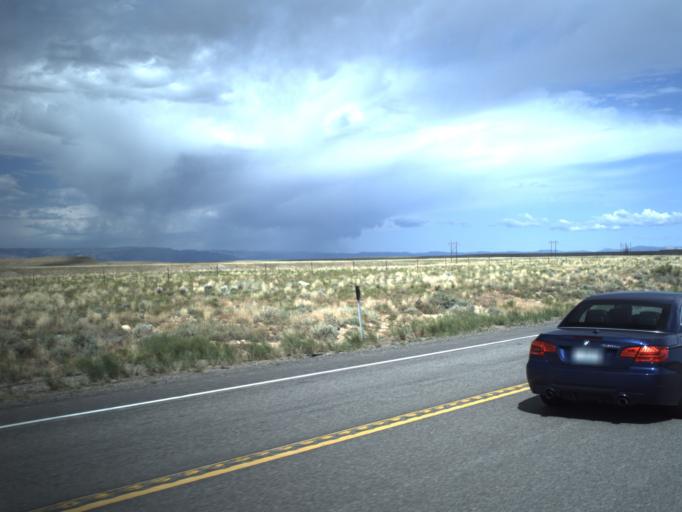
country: US
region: Utah
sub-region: Carbon County
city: East Carbon City
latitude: 39.4831
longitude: -110.5120
